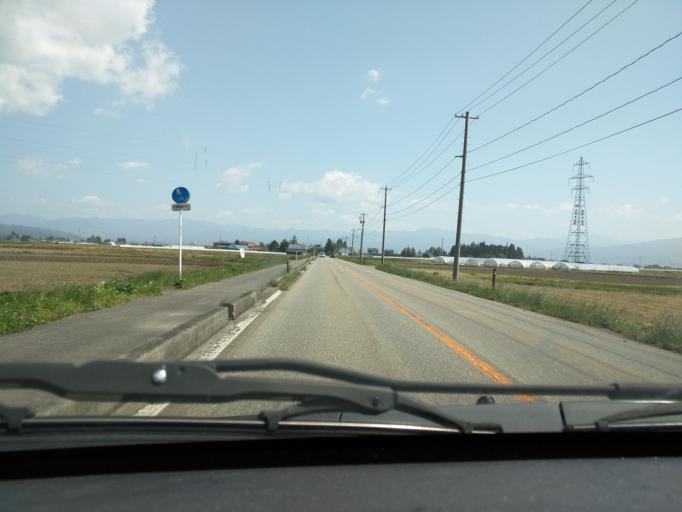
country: JP
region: Fukushima
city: Kitakata
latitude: 37.5743
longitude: 139.8302
